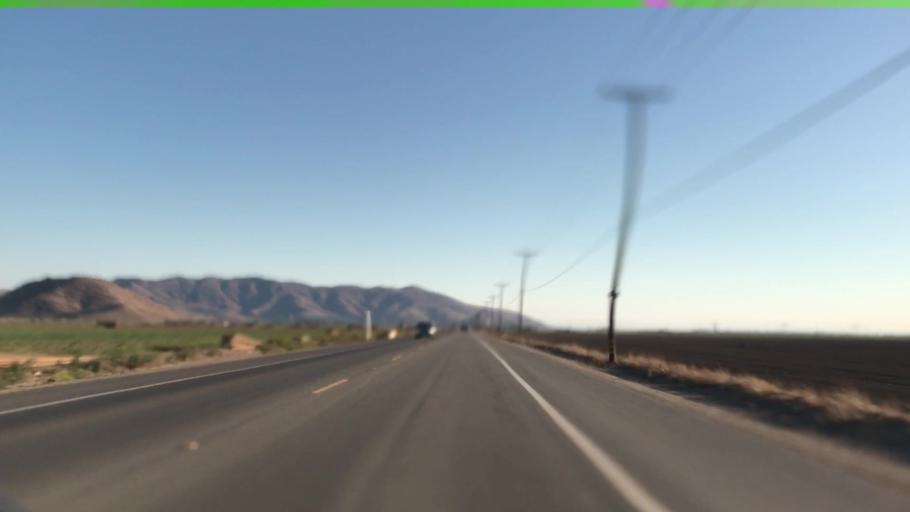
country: US
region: California
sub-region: Ventura County
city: Camarillo
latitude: 34.1883
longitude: -119.0699
